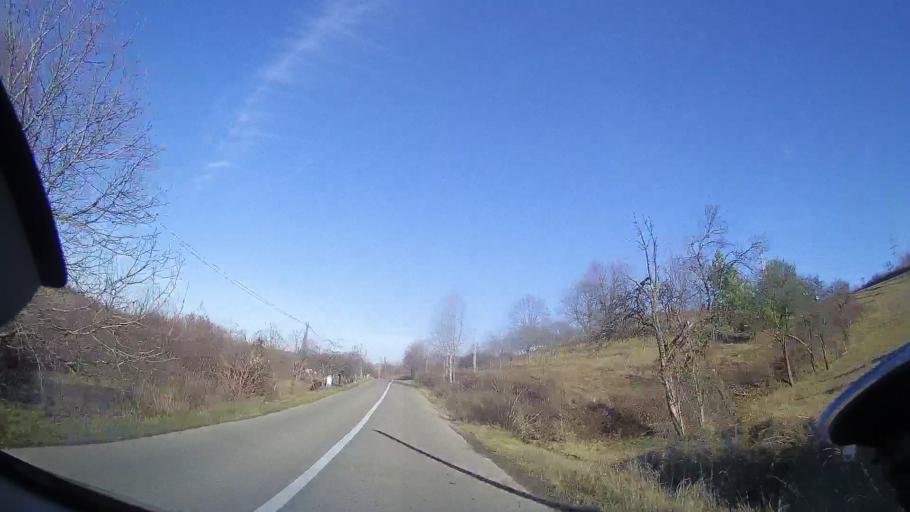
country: RO
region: Bihor
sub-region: Comuna Bratca
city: Bratca
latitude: 46.9359
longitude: 22.6040
